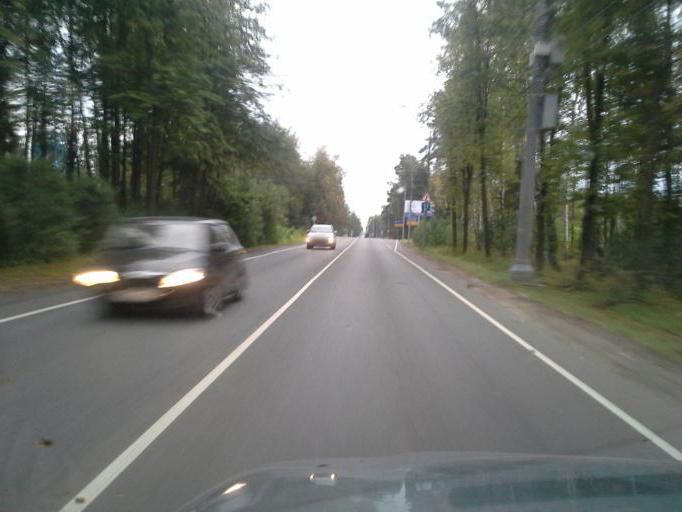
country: RU
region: Moskovskaya
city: Nazar'yevo
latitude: 55.6972
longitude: 37.0658
